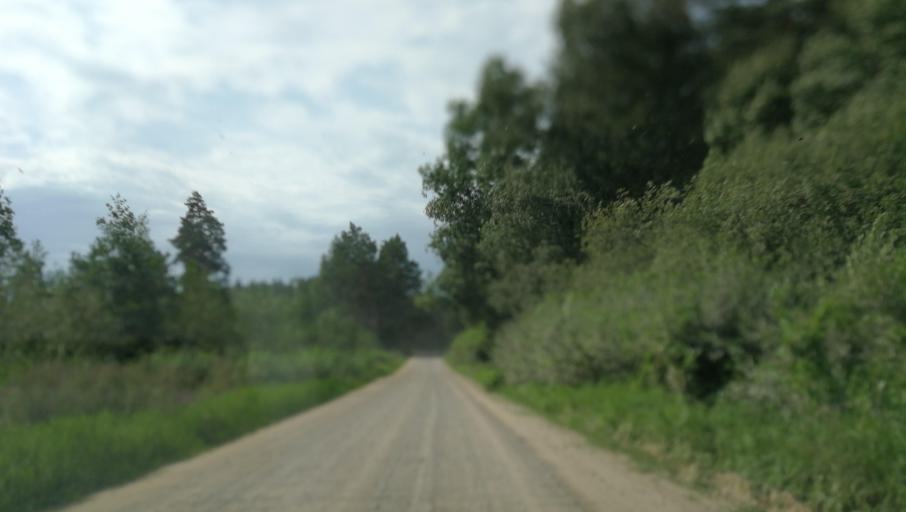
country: LV
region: Alsunga
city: Alsunga
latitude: 56.9728
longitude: 21.5554
